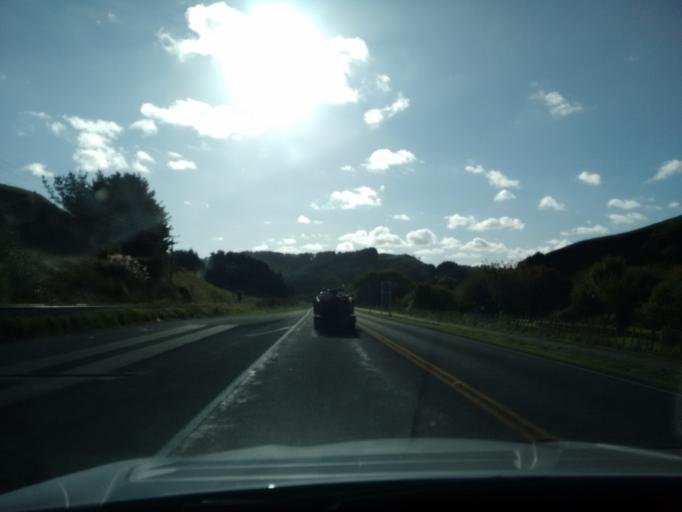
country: NZ
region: Manawatu-Wanganui
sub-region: Wanganui District
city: Wanganui
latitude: -39.8512
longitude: 174.9313
